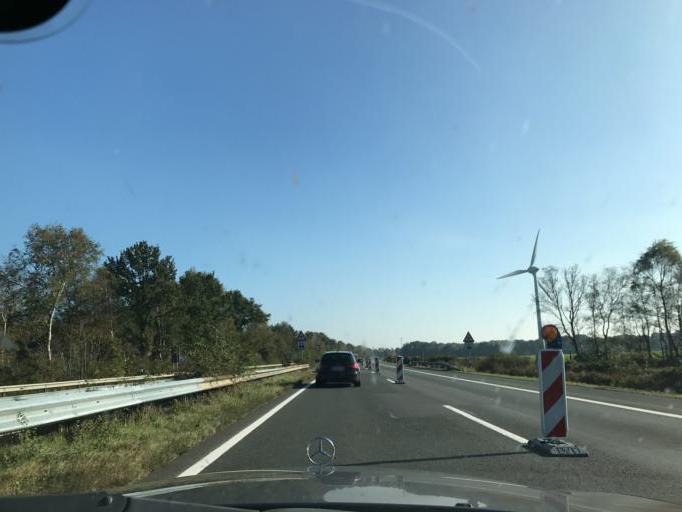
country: DE
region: Lower Saxony
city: Wiefelstede
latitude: 53.2013
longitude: 8.0884
